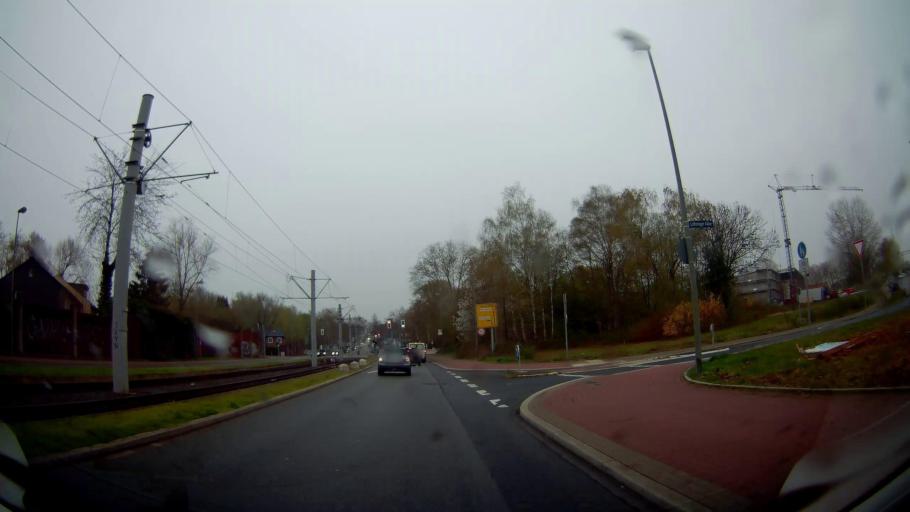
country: DE
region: North Rhine-Westphalia
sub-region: Regierungsbezirk Arnsberg
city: Herne
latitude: 51.5145
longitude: 7.2702
